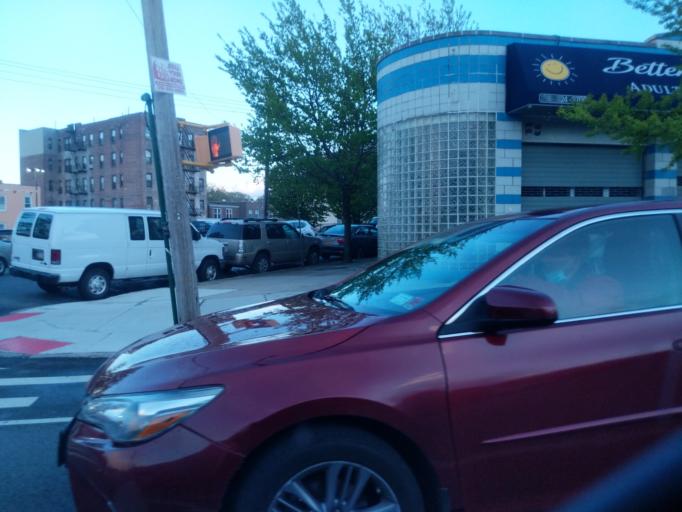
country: US
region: New York
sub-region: Bronx
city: The Bronx
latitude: 40.8645
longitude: -73.8637
